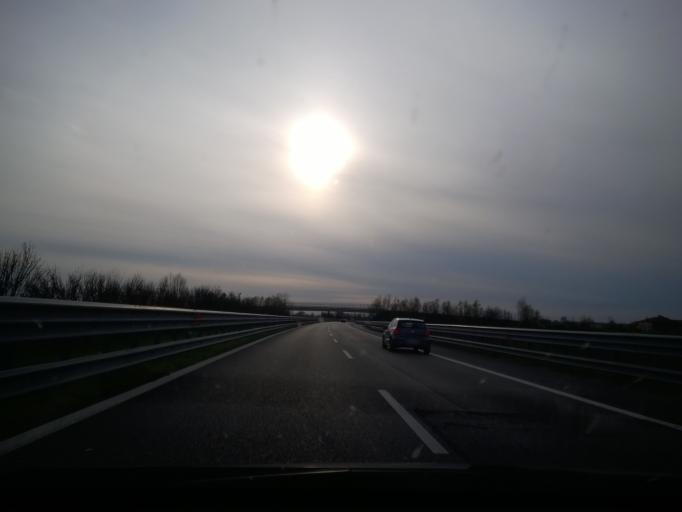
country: IT
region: Emilia-Romagna
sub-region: Provincia di Piacenza
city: Caorso
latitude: 45.0459
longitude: 9.8426
